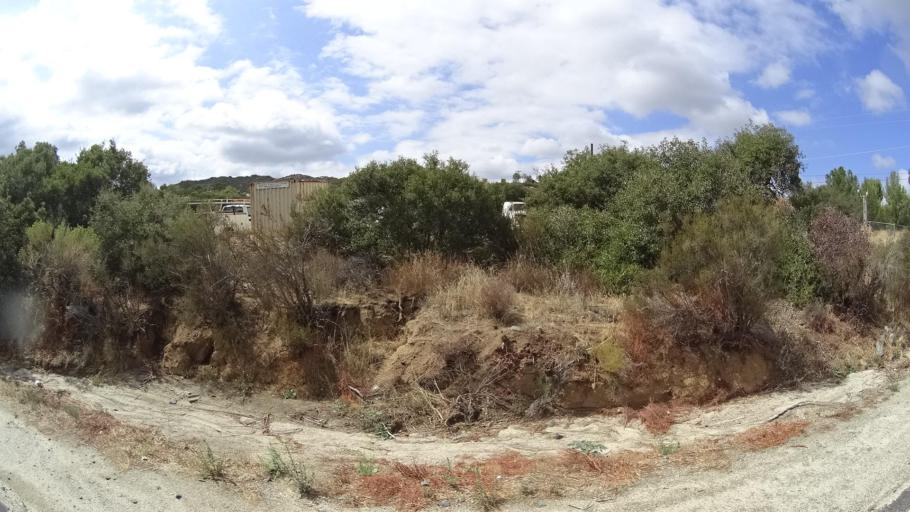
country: US
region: California
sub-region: San Diego County
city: Campo
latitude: 32.6723
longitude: -116.4885
